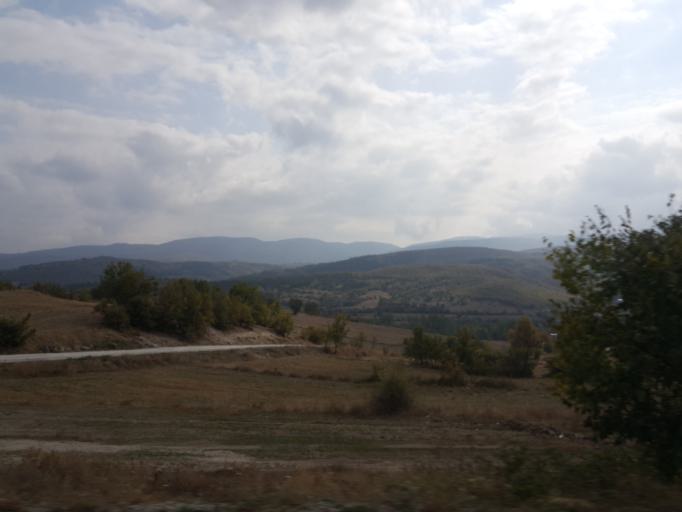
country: TR
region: Sinop
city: Sarayduzu
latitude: 41.3284
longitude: 34.7670
